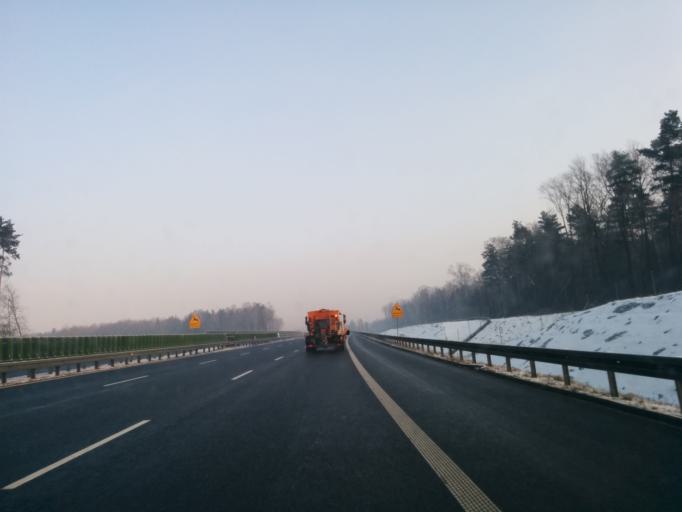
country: PL
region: Silesian Voivodeship
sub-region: Gliwice
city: Gliwice
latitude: 50.3186
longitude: 18.7262
